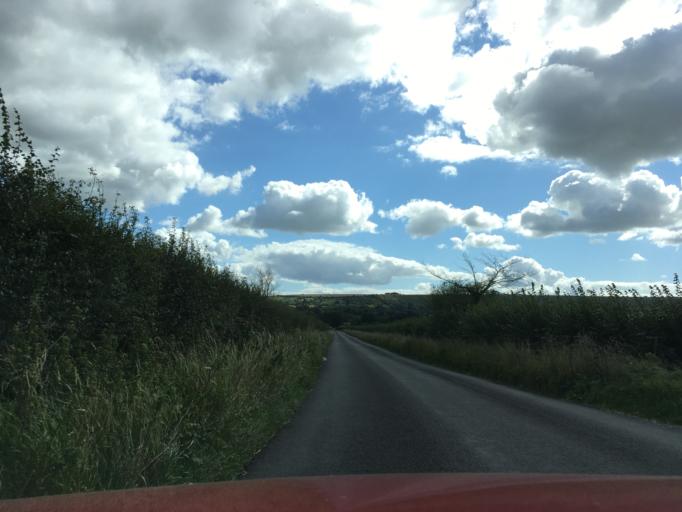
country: GB
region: England
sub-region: Wiltshire
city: Bratton
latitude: 51.2848
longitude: -2.1286
